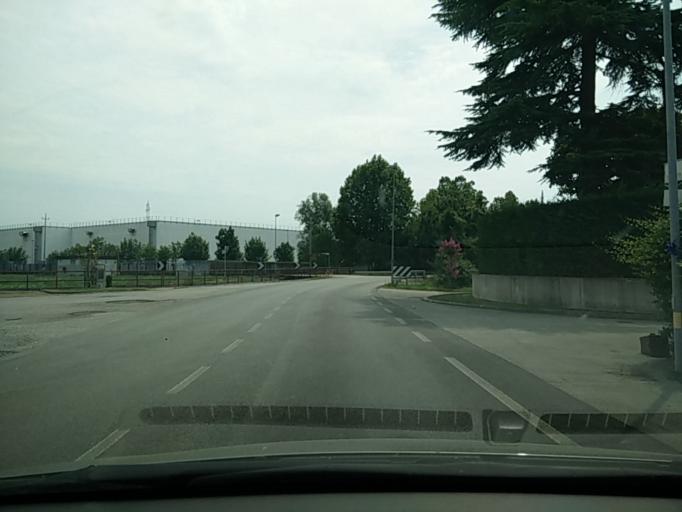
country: IT
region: Veneto
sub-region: Provincia di Treviso
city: Mignagola
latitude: 45.6861
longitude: 12.3248
